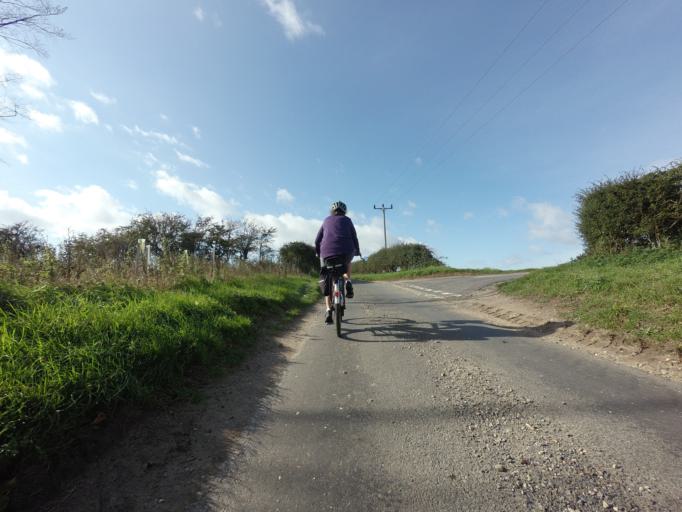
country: GB
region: England
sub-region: Norfolk
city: Hunstanton
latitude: 52.9363
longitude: 0.6260
